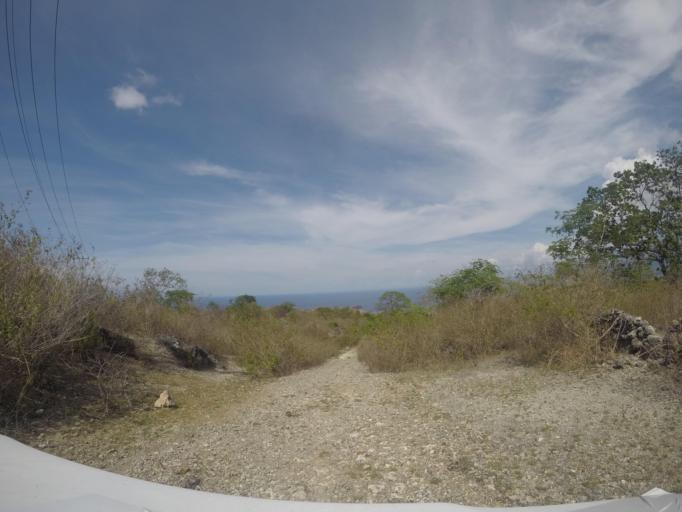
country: TL
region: Baucau
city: Baucau
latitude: -8.4671
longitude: 126.4678
